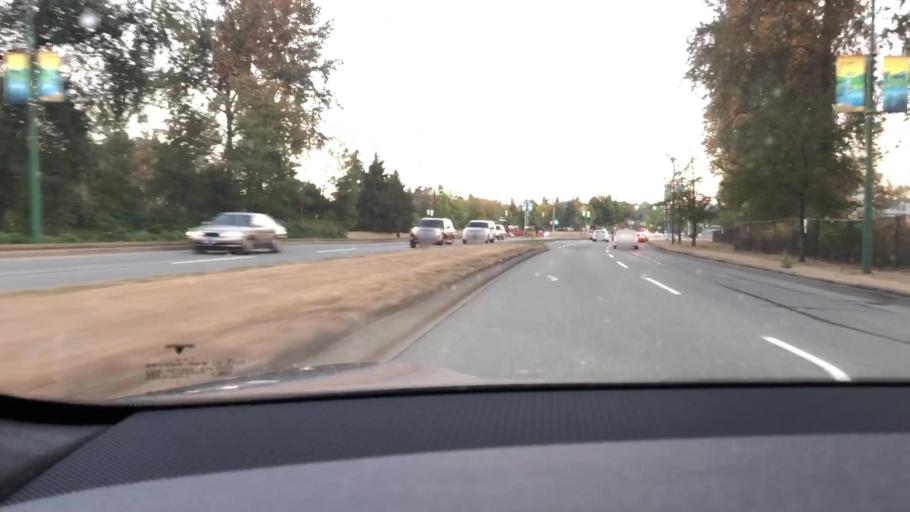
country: CA
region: British Columbia
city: Burnaby
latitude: 49.2588
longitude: -122.9627
